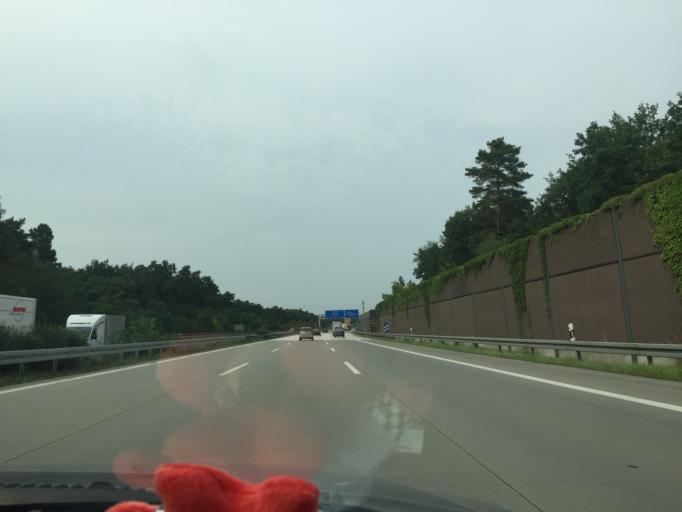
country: DE
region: Brandenburg
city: Grunheide
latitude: 52.4166
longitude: 13.7854
